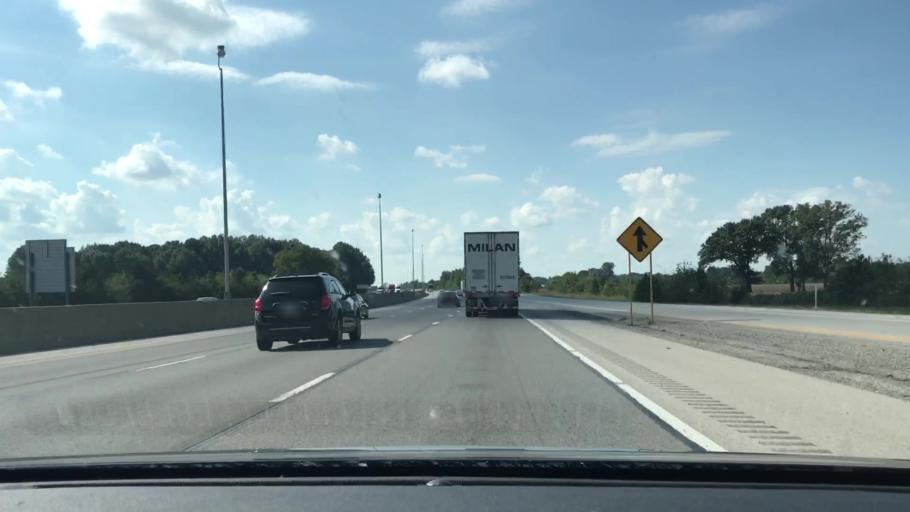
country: US
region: Kentucky
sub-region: Warren County
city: Plano
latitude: 36.9026
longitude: -86.4365
